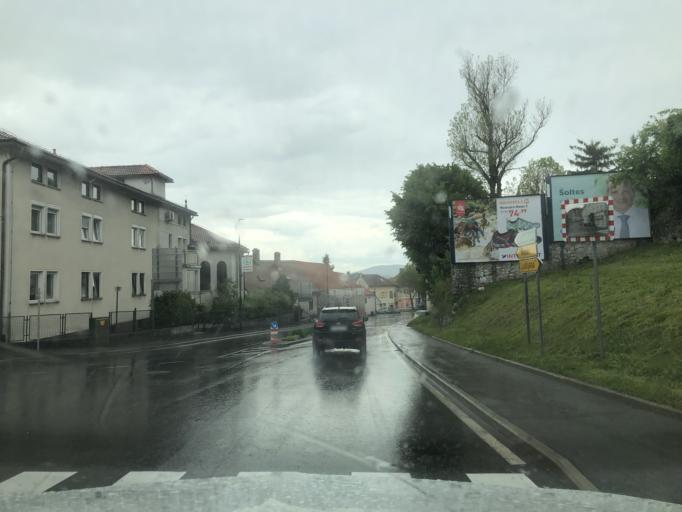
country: SI
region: Postojna
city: Postojna
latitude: 45.7775
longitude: 14.2159
